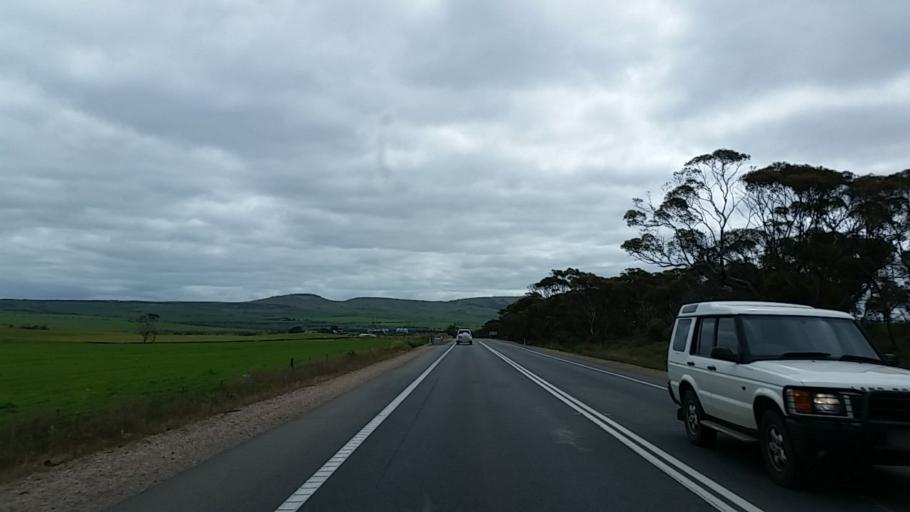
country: AU
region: South Australia
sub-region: Wakefield
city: Balaklava
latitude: -33.9634
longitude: 138.1812
